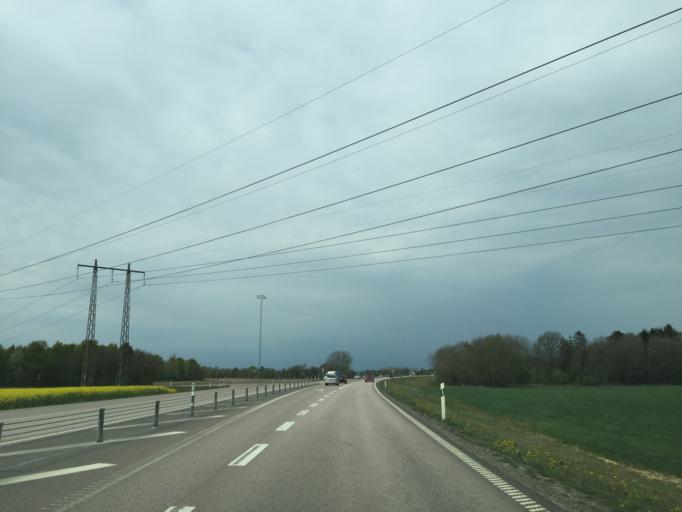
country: SE
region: Skane
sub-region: Helsingborg
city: Helsingborg
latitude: 56.0945
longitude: 12.6820
